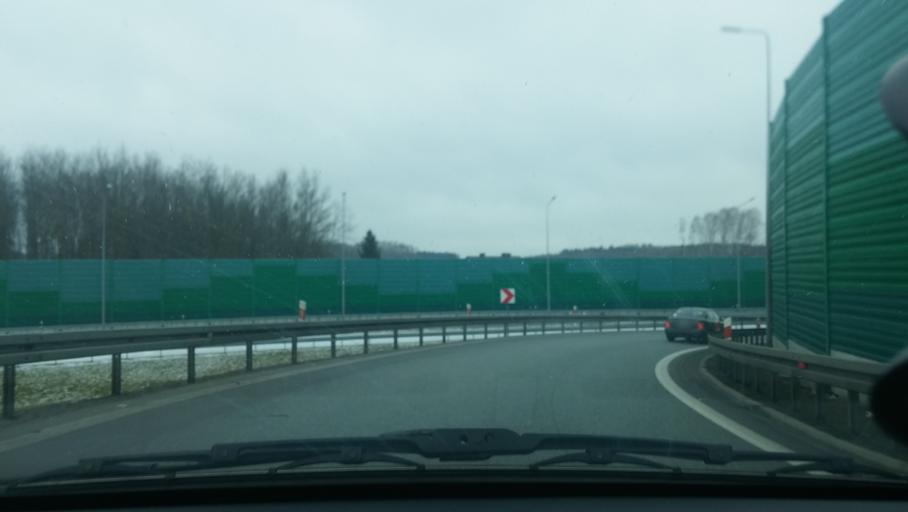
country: PL
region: Masovian Voivodeship
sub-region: Powiat minski
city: Kaluszyn
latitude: 52.1977
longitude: 21.7737
